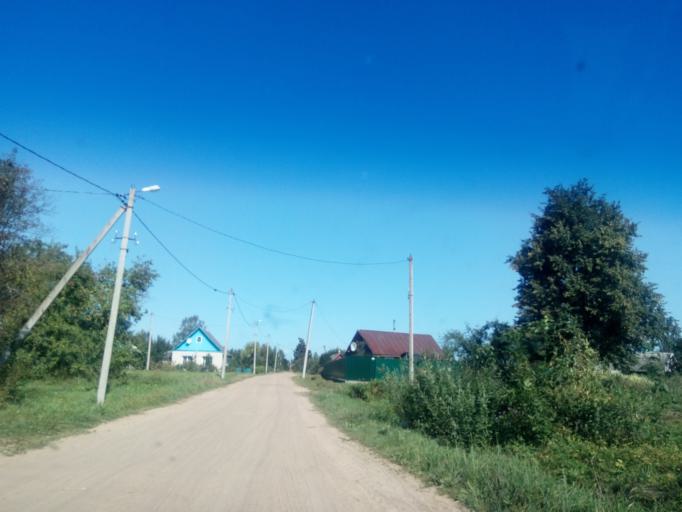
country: BY
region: Vitebsk
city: Dzisna
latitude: 55.6654
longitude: 28.3253
